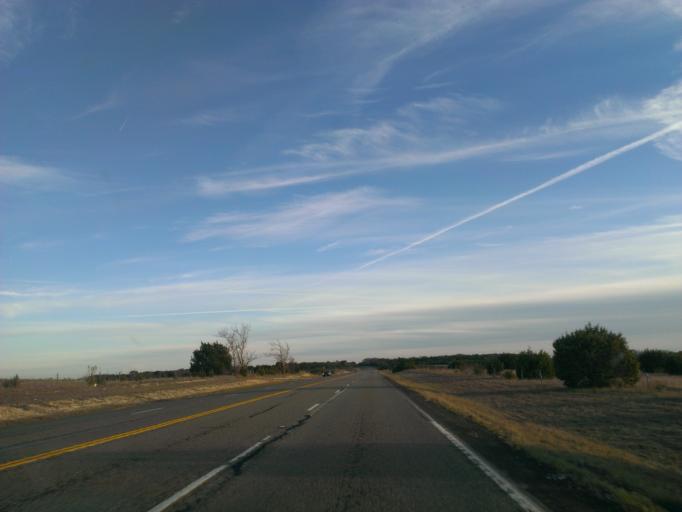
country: US
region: Texas
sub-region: Burnet County
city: Bertram
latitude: 30.9001
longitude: -97.9667
